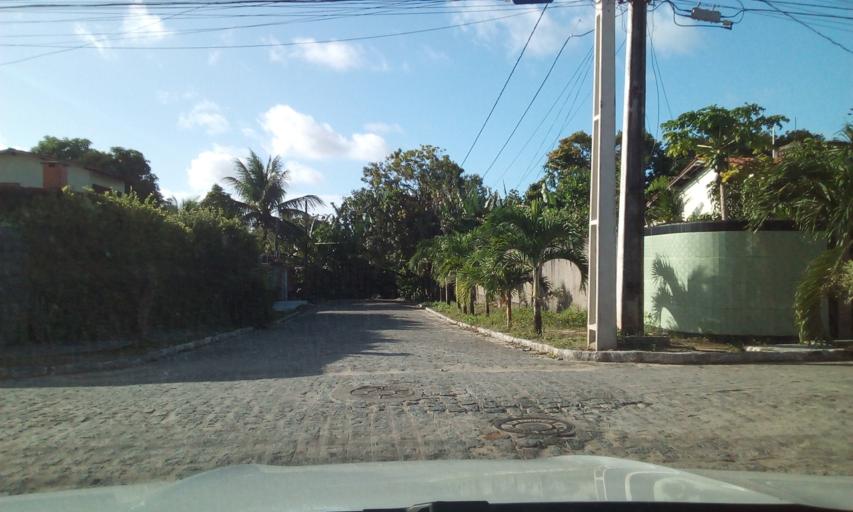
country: BR
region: Paraiba
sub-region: Joao Pessoa
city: Joao Pessoa
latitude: -7.1575
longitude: -34.8332
